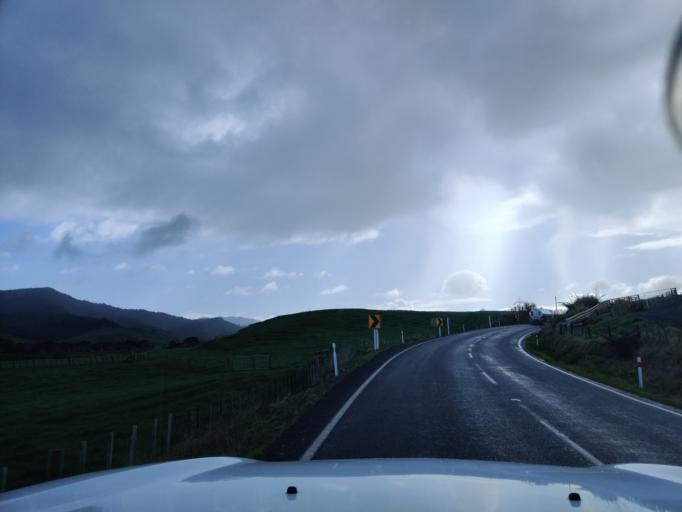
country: NZ
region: Waikato
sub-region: Waikato District
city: Ngaruawahia
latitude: -37.5826
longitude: 175.2166
